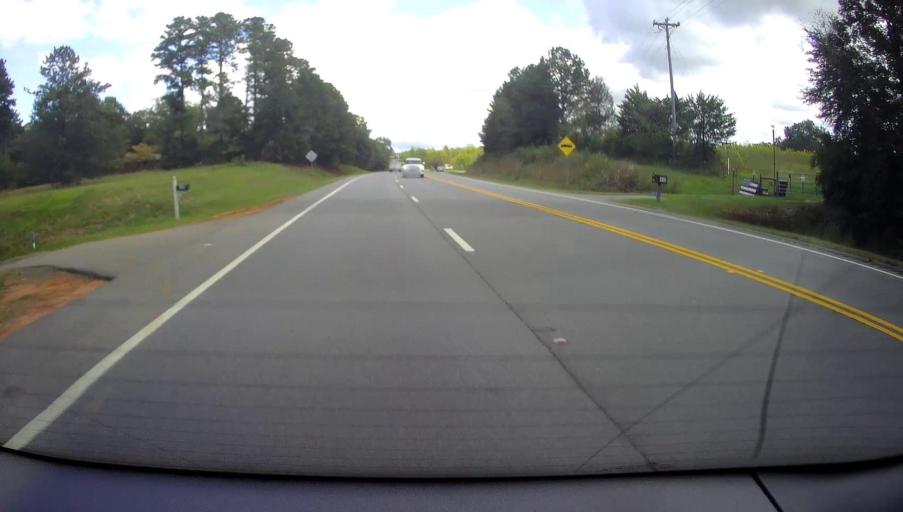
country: US
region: Georgia
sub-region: Baldwin County
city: Milledgeville
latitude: 33.0716
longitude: -83.3492
